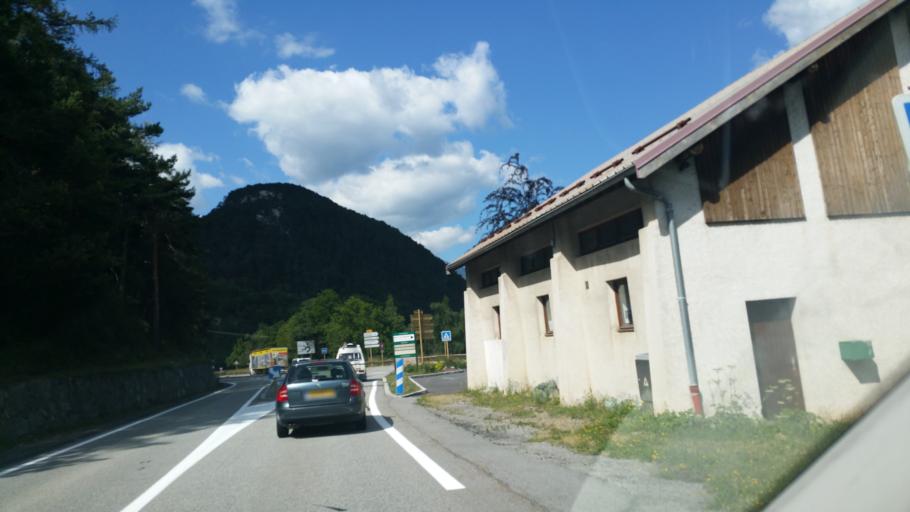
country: FR
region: Rhone-Alpes
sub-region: Departement de la Savoie
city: Modane
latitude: 45.2069
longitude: 6.7080
